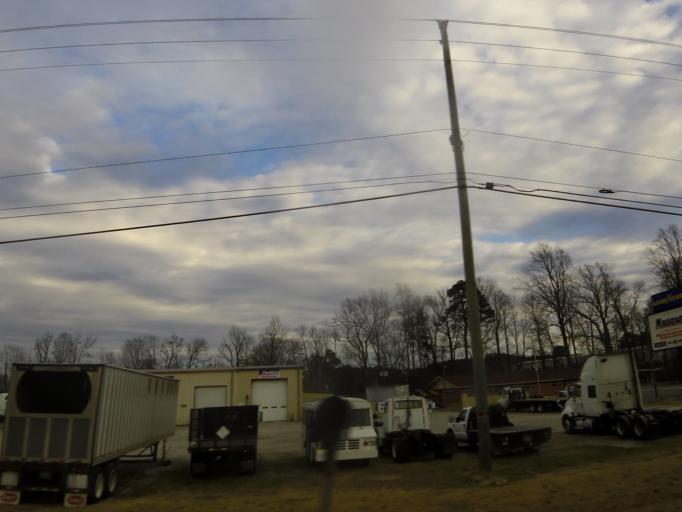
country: US
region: North Carolina
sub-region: Nash County
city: Rocky Mount
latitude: 36.0022
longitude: -77.7749
